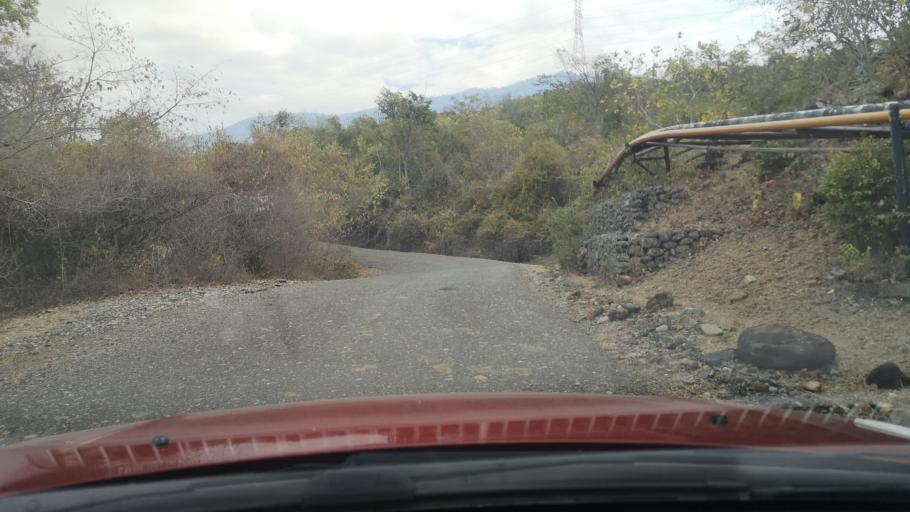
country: CO
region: Huila
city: Neiva
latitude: 2.9566
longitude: -75.3425
